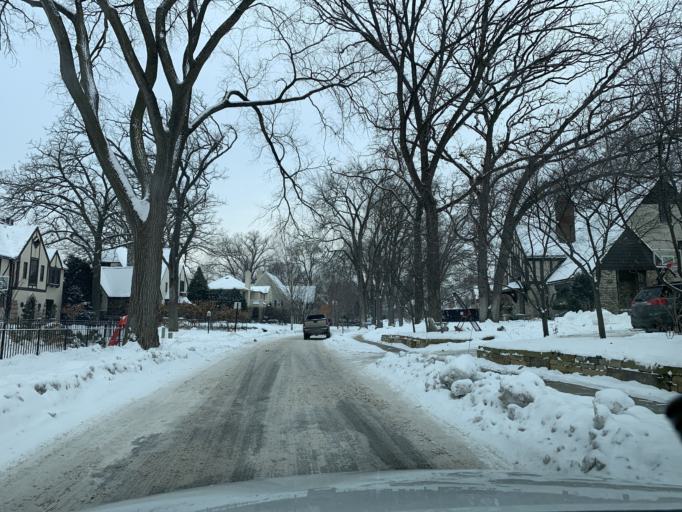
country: US
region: Minnesota
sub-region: Hennepin County
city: Edina
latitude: 44.9182
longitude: -93.3445
